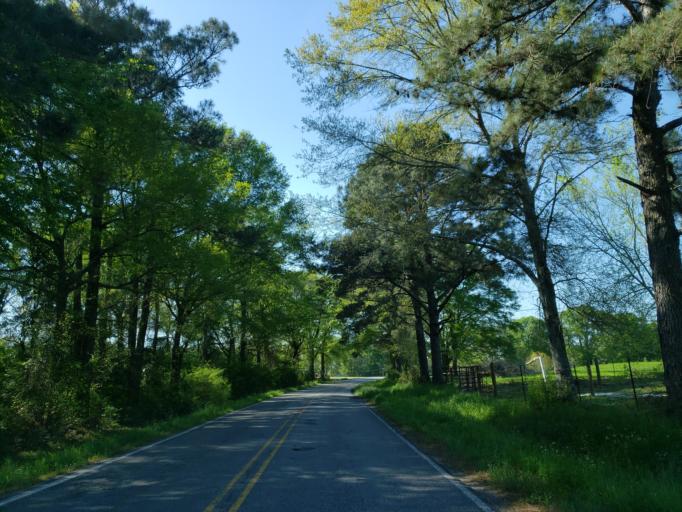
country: US
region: Mississippi
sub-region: Forrest County
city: Rawls Springs
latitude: 31.5367
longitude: -89.3626
